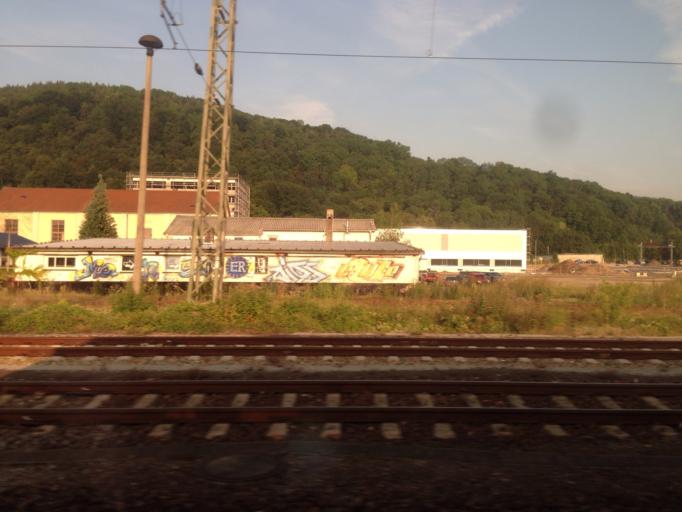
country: DE
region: Thuringia
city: Sulza
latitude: 50.8862
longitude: 11.5926
